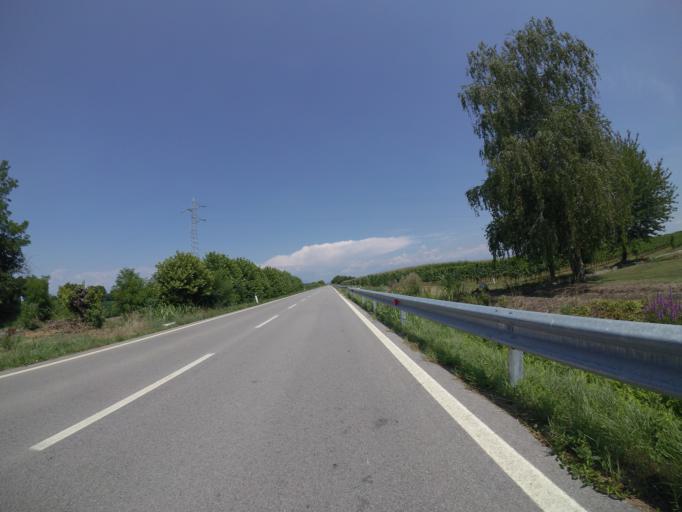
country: IT
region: Friuli Venezia Giulia
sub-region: Provincia di Udine
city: Bertiolo
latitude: 45.9547
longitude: 13.0550
